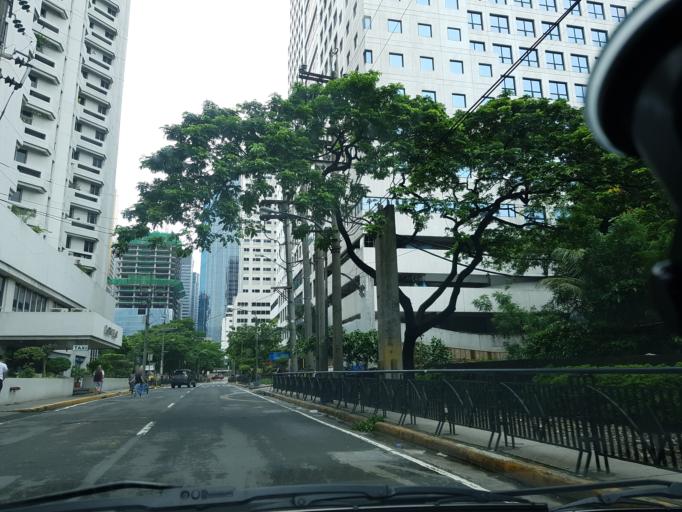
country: PH
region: Metro Manila
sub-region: Pasig
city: Pasig City
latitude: 14.5818
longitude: 121.0611
